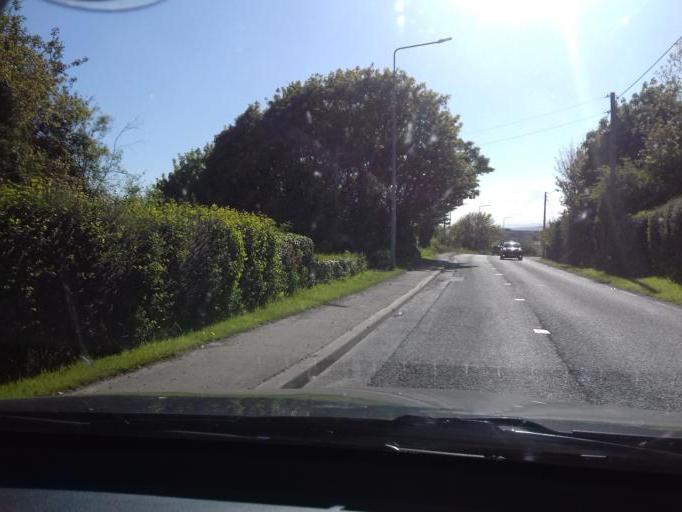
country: IE
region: Munster
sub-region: Waterford
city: Waterford
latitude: 52.2812
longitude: -7.1537
